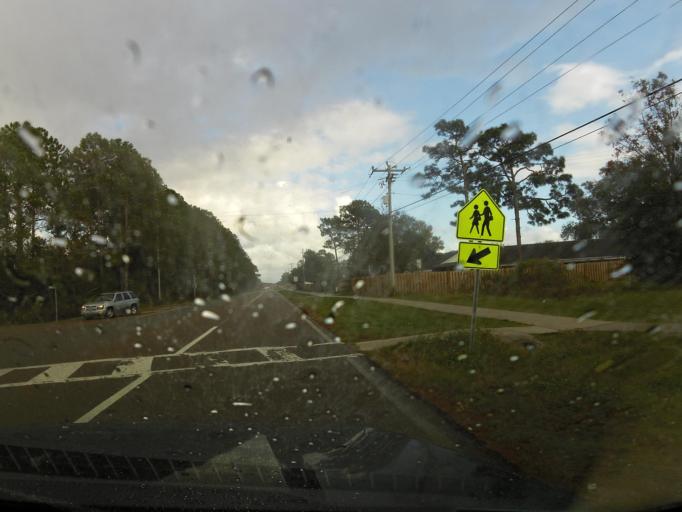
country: US
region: Florida
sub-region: Clay County
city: Asbury Lake
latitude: 30.0461
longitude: -81.8006
